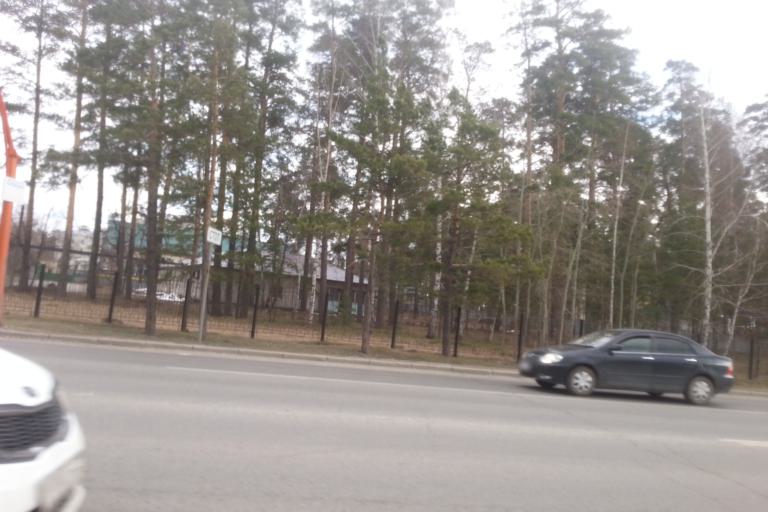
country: RU
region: Altai Krai
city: Zaton
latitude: 53.2817
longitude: 83.7495
